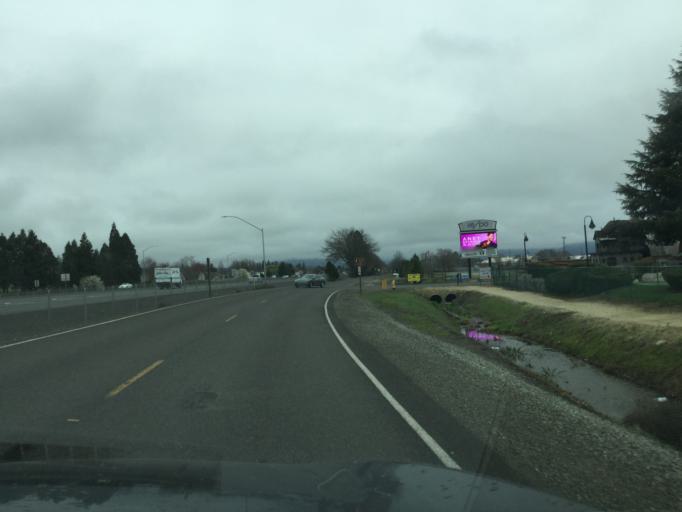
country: US
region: Oregon
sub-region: Jackson County
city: Central Point
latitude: 42.3803
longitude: -122.9056
